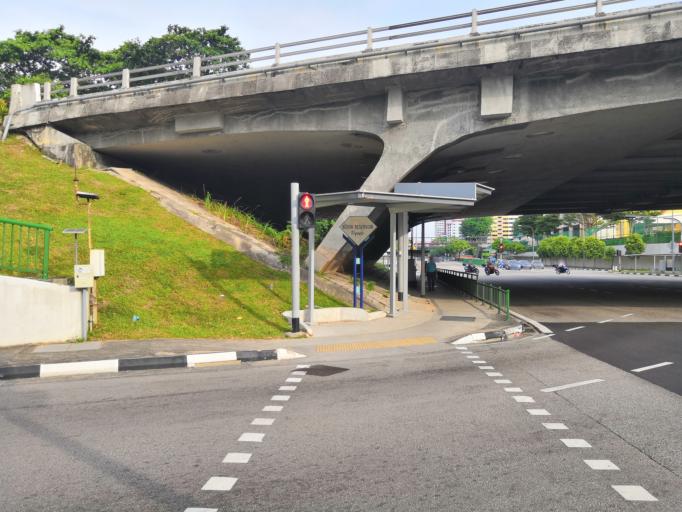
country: SG
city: Singapore
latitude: 1.3357
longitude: 103.9337
